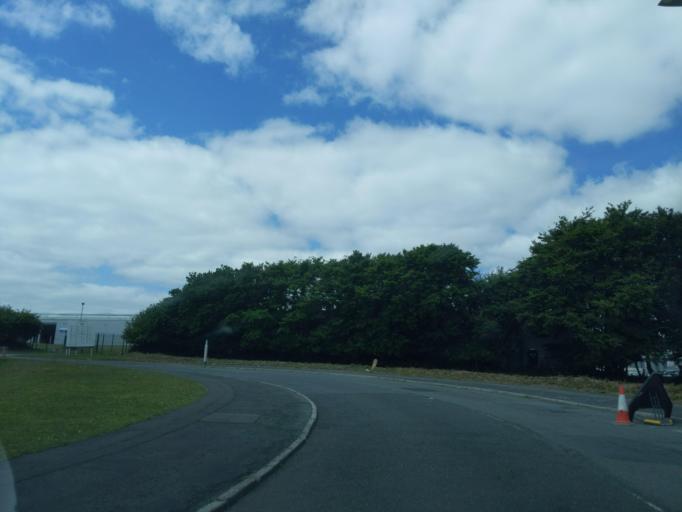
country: GB
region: England
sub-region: Devon
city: Plympton
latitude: 50.4207
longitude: -4.0914
